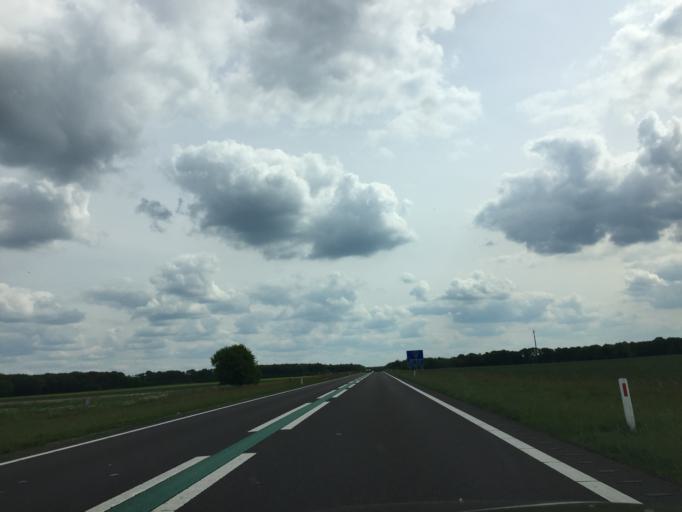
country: NL
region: Drenthe
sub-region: Gemeente Aa en Hunze
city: Anloo
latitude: 53.0185
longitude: 6.7481
